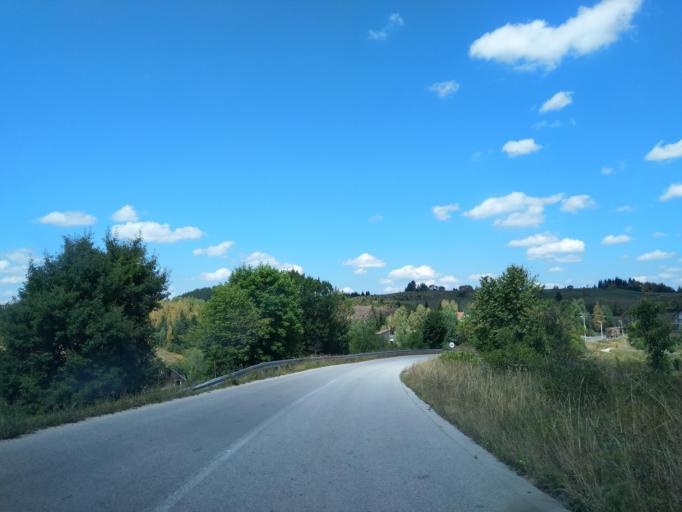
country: RS
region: Central Serbia
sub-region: Zlatiborski Okrug
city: Nova Varos
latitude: 43.4243
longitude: 19.8271
